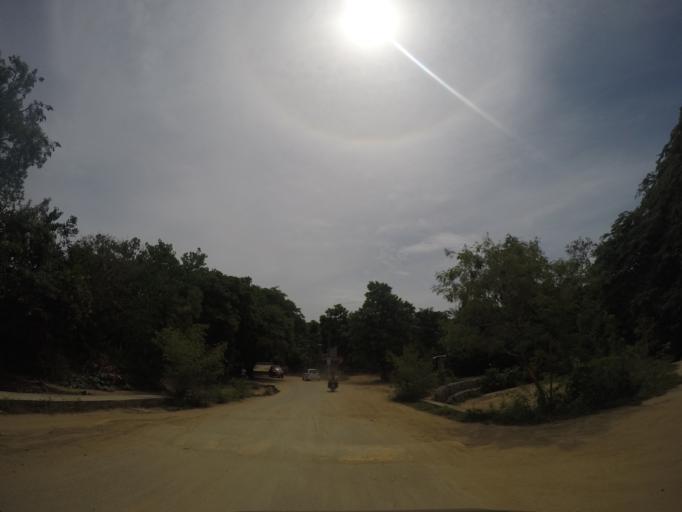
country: MX
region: Oaxaca
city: Santa Maria Tonameca
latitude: 15.6678
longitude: -96.5238
